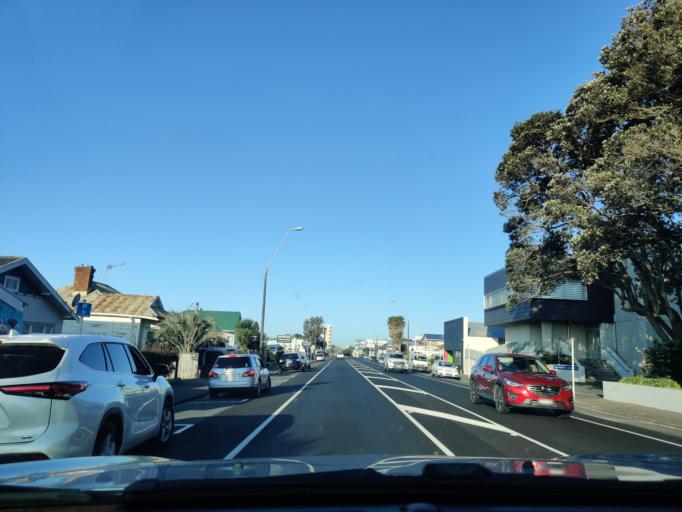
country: NZ
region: Taranaki
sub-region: New Plymouth District
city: New Plymouth
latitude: -39.0582
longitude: 174.0632
